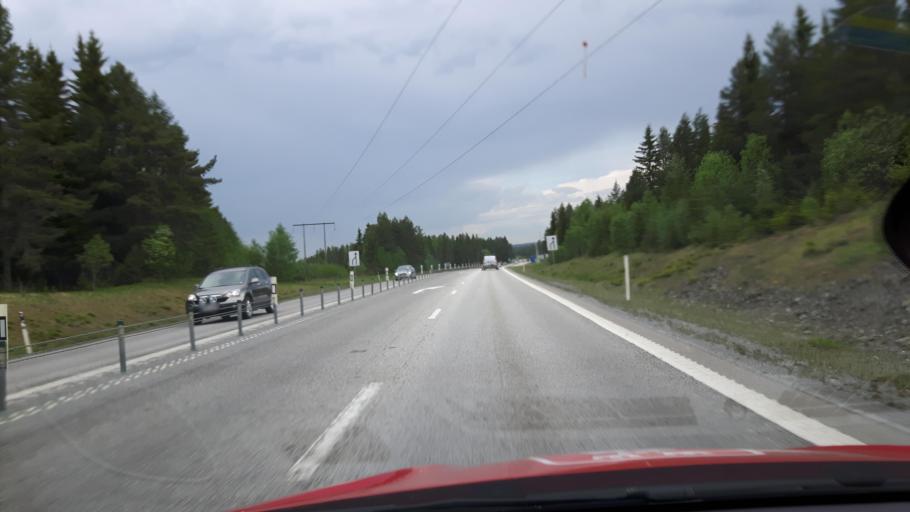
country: SE
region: Jaemtland
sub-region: OEstersunds Kommun
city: Brunflo
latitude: 63.1221
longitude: 14.7955
